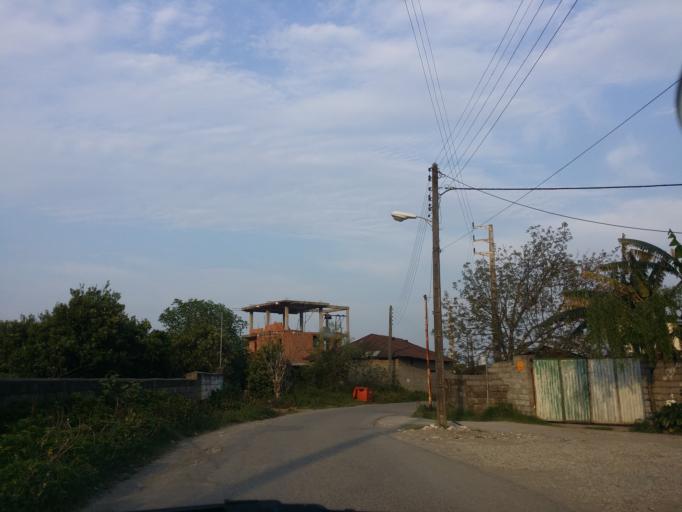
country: IR
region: Mazandaran
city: Chalus
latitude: 36.6655
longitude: 51.3732
